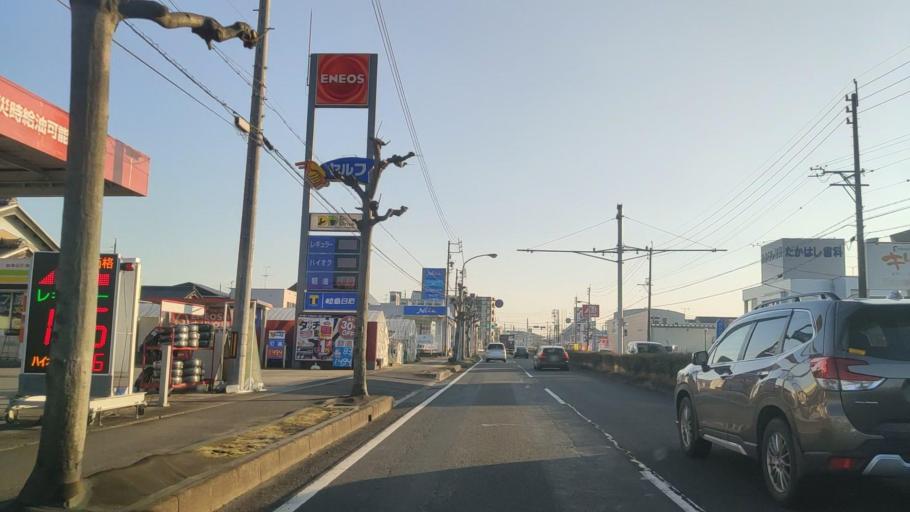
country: JP
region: Gifu
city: Gifu-shi
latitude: 35.4412
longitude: 136.7387
